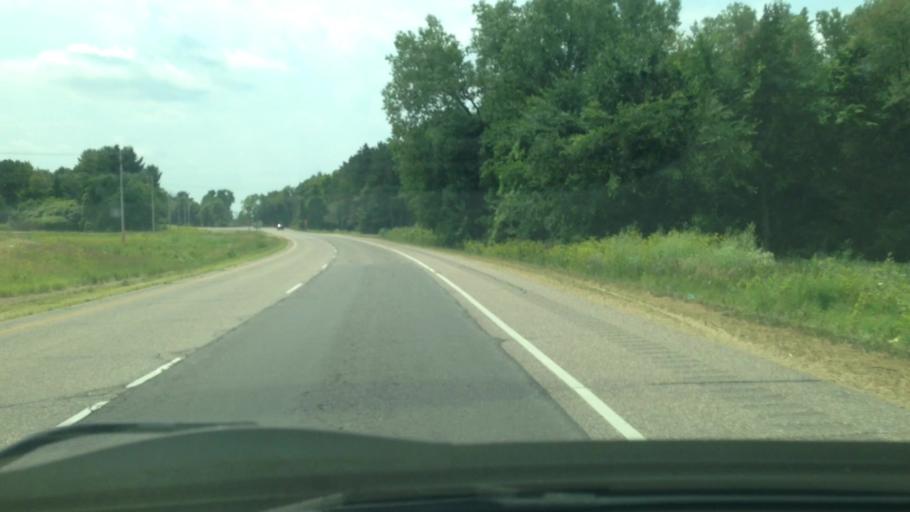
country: US
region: Wisconsin
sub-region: Sauk County
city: Prairie du Sac
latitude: 43.3558
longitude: -89.7690
